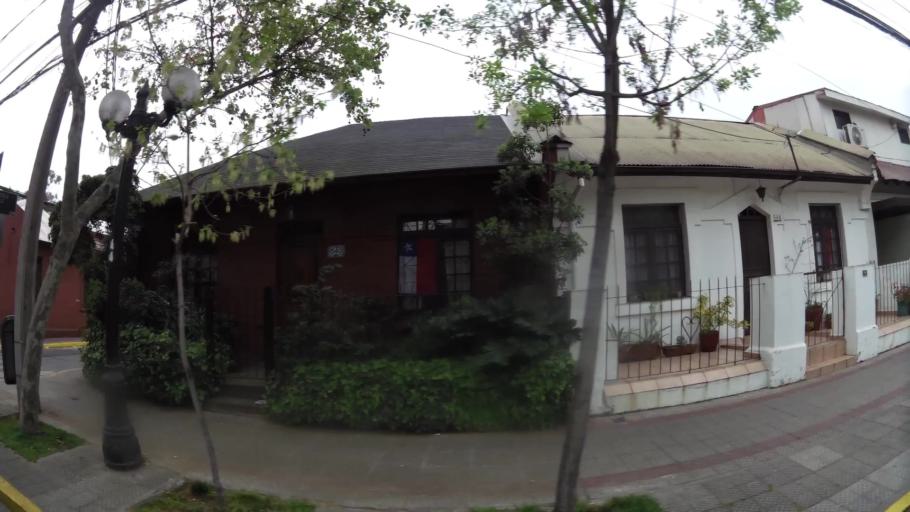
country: CL
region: Santiago Metropolitan
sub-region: Provincia de Santiago
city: Santiago
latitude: -33.4365
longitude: -70.6224
